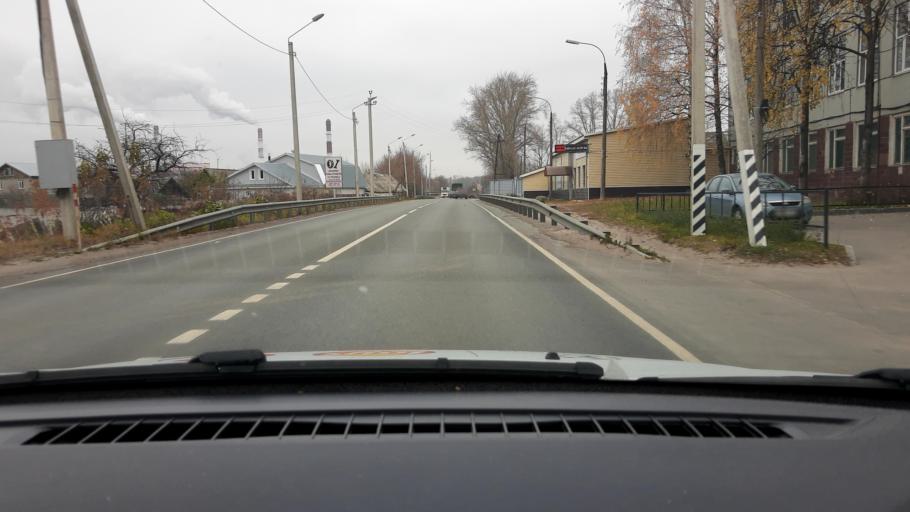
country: RU
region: Nizjnij Novgorod
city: Novaya Balakhna
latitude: 56.4904
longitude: 43.5962
